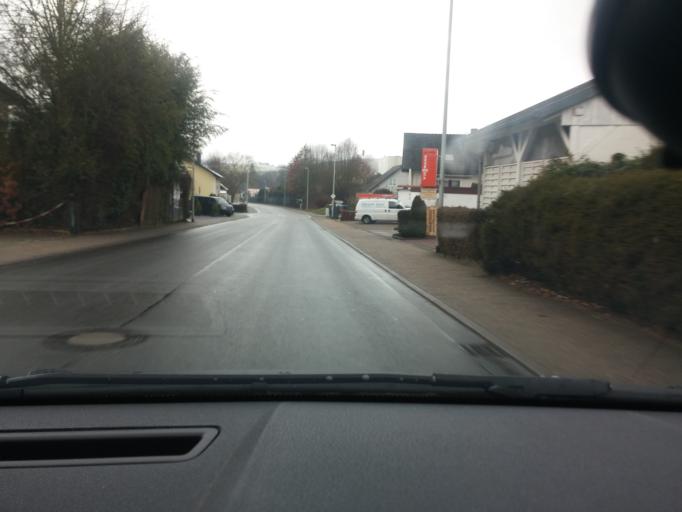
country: DE
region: Hesse
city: Michelstadt
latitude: 49.6865
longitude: 9.0098
